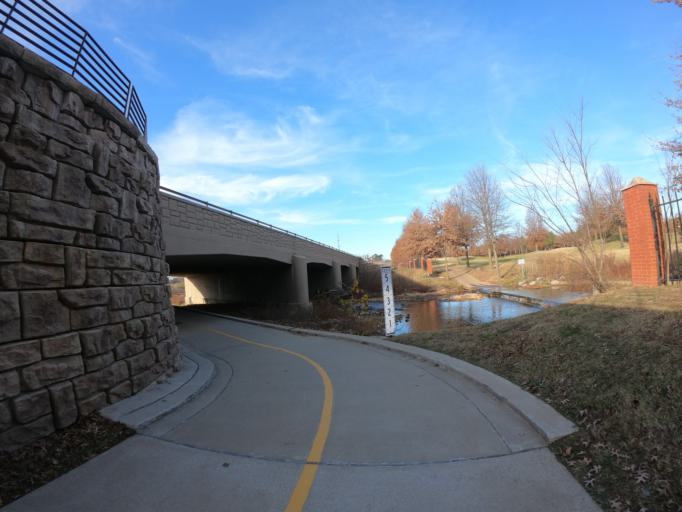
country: US
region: Arkansas
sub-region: Benton County
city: Lowell
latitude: 36.2915
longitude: -94.1716
